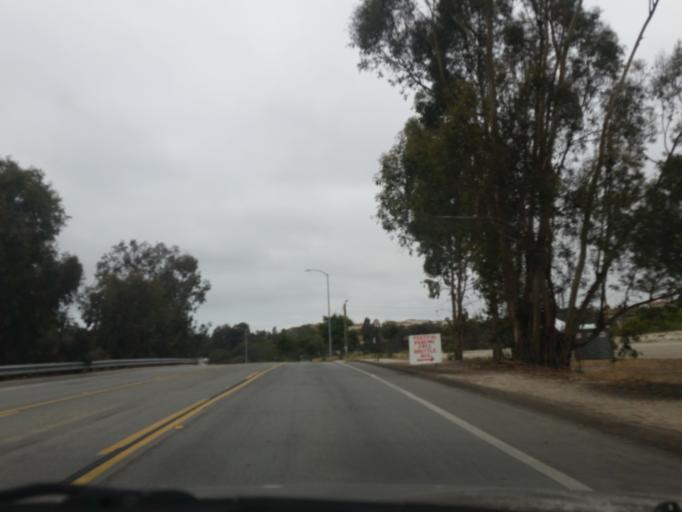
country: US
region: California
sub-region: San Luis Obispo County
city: Arroyo Grande
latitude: 35.1227
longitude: -120.5856
